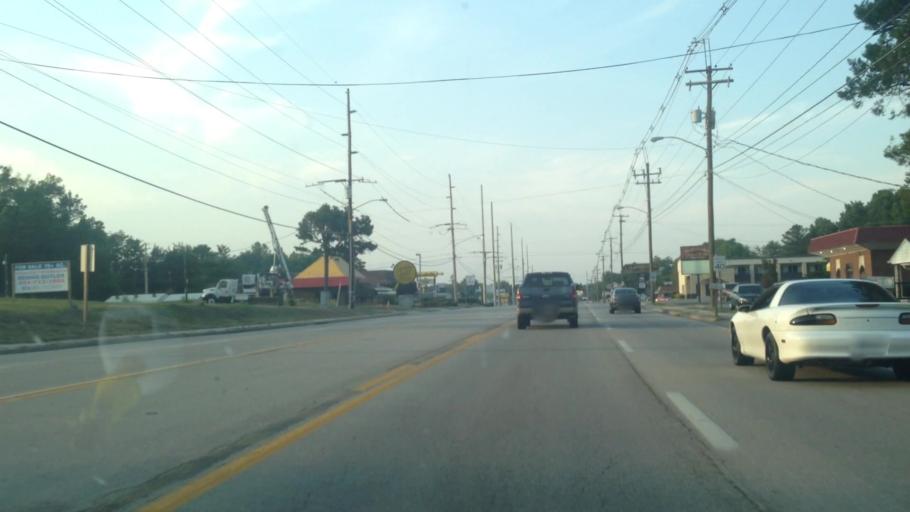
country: US
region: Virginia
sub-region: City of Danville
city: Danville
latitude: 36.6209
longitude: -79.4054
